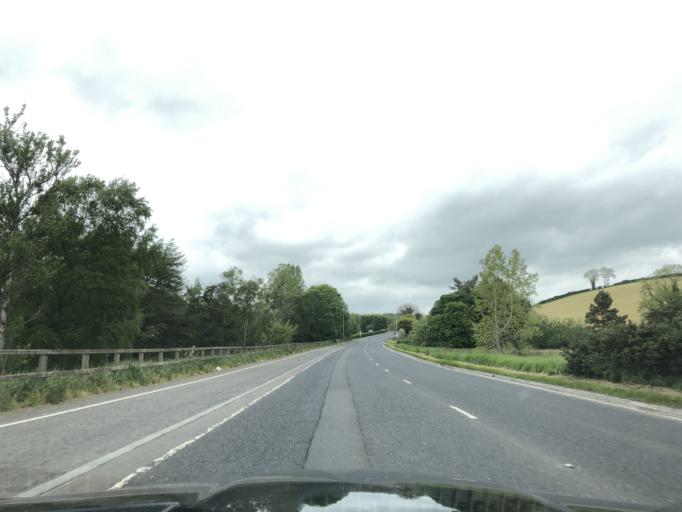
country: GB
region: Northern Ireland
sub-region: Down District
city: Downpatrick
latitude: 54.3408
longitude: -5.7289
